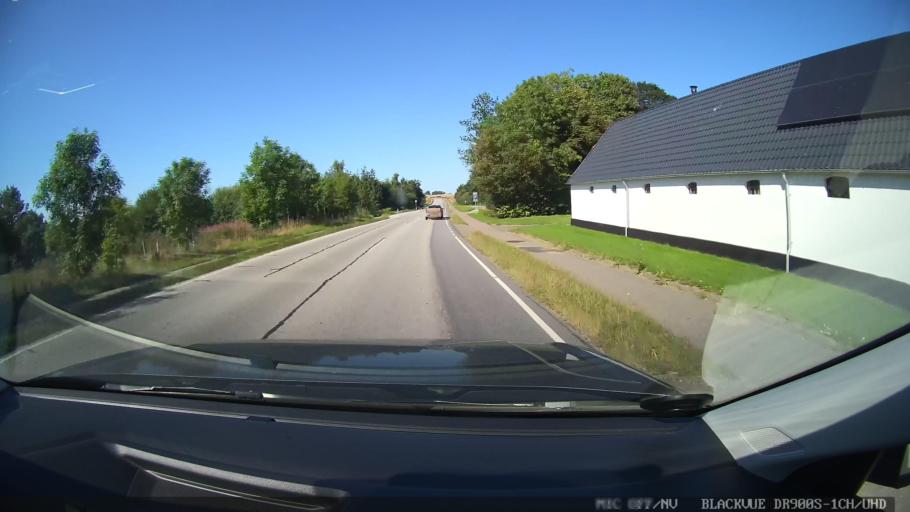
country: DK
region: Central Jutland
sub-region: Randers Kommune
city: Spentrup
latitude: 56.5142
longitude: 10.0166
